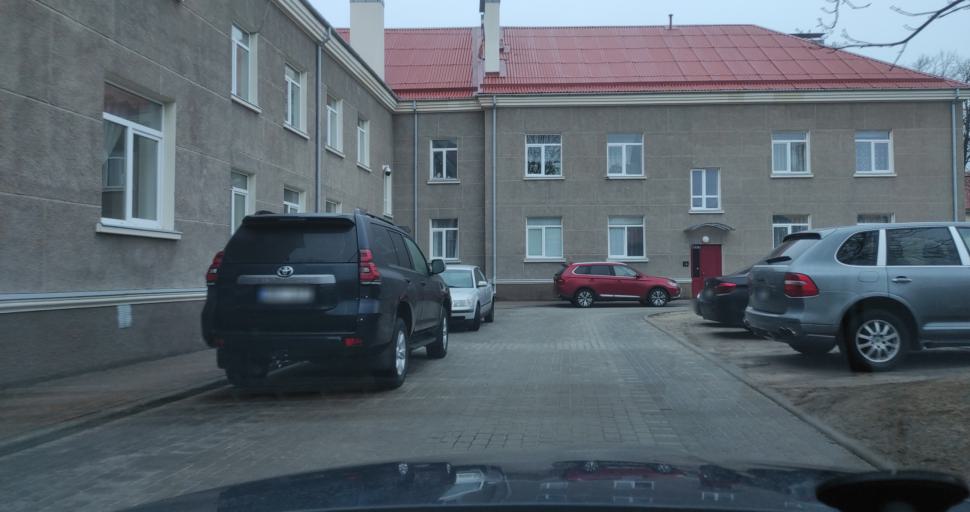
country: LV
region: Ventspils
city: Ventspils
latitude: 57.3891
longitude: 21.5499
